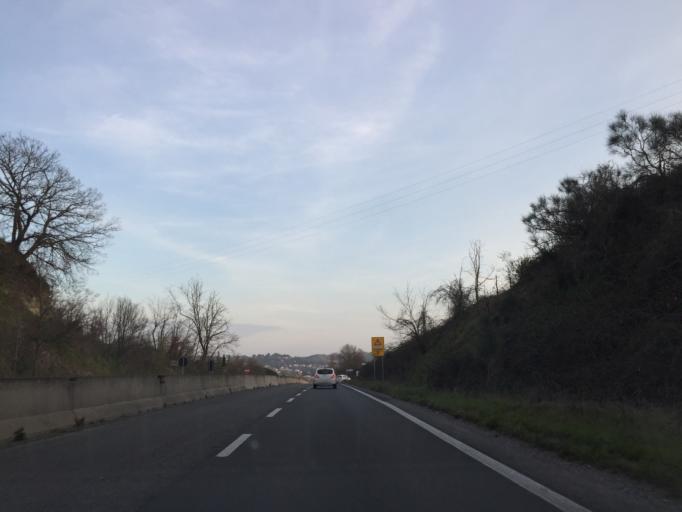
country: IT
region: Latium
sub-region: Citta metropolitana di Roma Capitale
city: Campagnano di Roma
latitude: 42.1355
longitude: 12.3532
